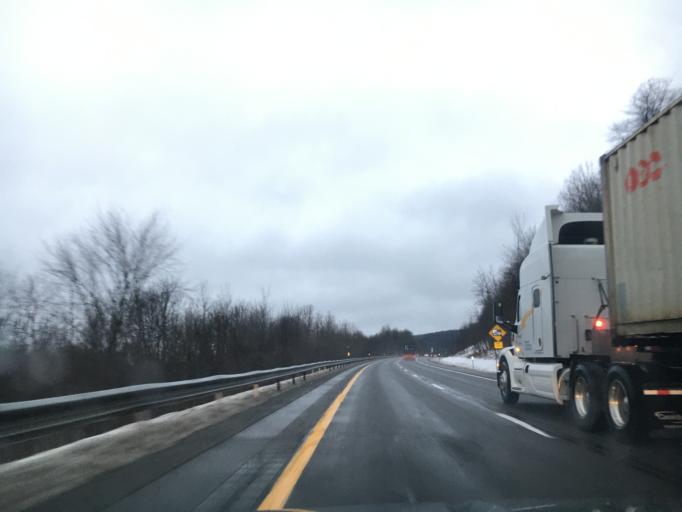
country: US
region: New York
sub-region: Cortland County
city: McGraw
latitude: 42.5091
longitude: -76.0786
